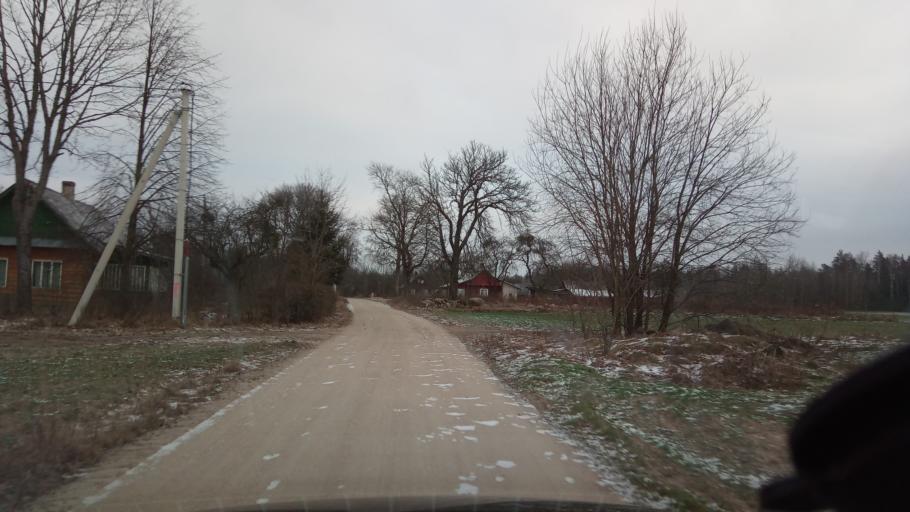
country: LT
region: Alytaus apskritis
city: Varena
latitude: 54.1264
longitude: 24.7051
